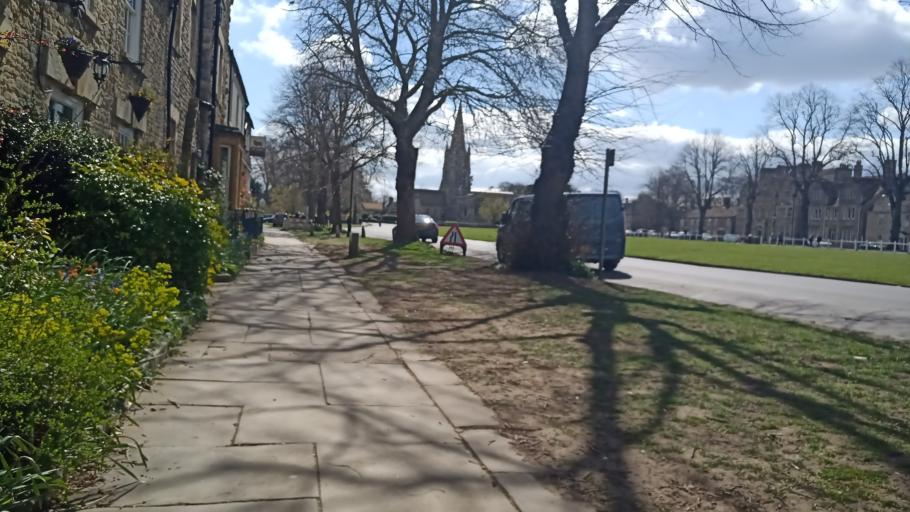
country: GB
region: England
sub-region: Oxfordshire
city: Witney
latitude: 51.7830
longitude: -1.4853
